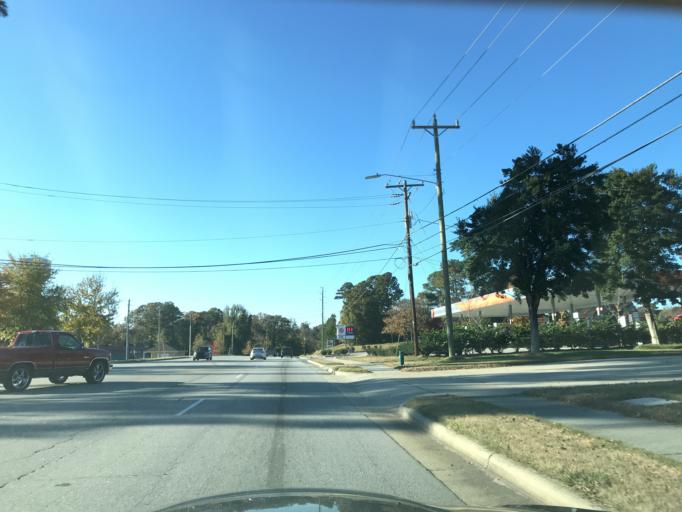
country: US
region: North Carolina
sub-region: Wake County
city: Raleigh
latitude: 35.7687
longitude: -78.5799
